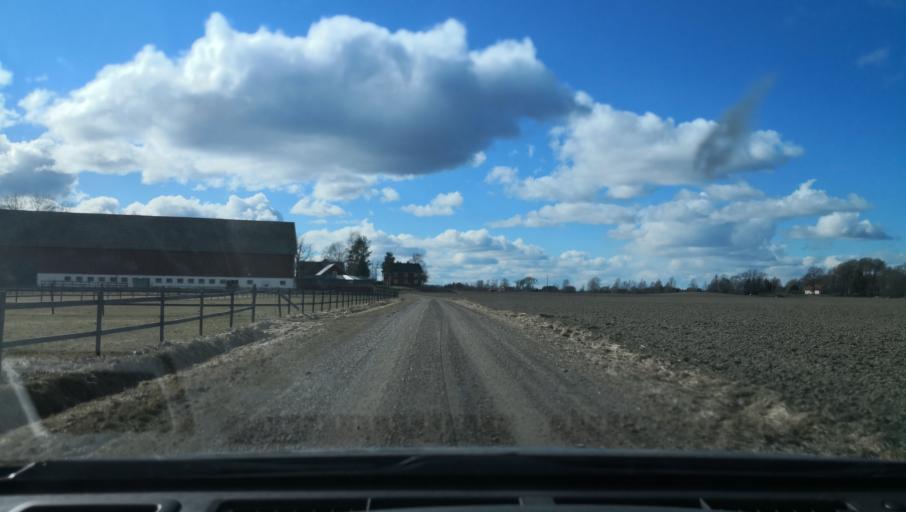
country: SE
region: OErebro
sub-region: Lindesbergs Kommun
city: Fellingsbro
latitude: 59.4140
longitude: 15.6416
